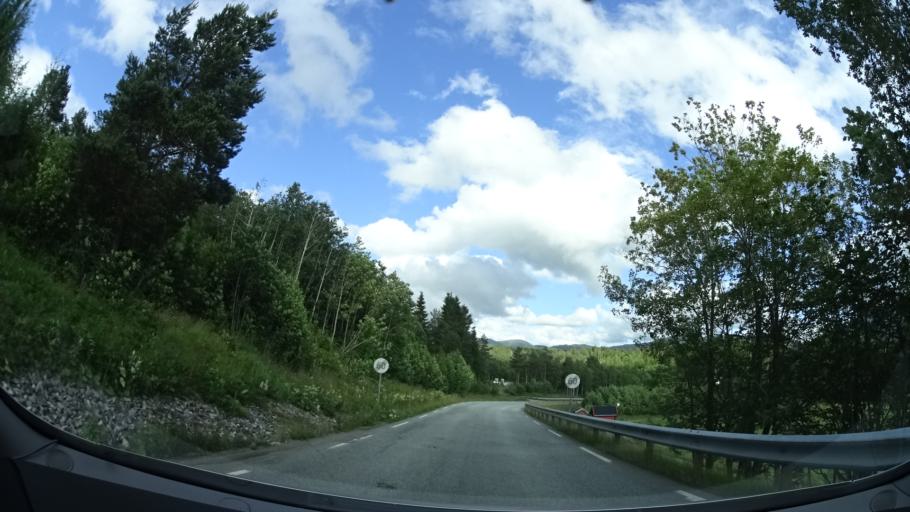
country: NO
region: More og Romsdal
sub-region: Halsa
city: Liaboen
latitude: 63.1177
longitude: 8.3171
